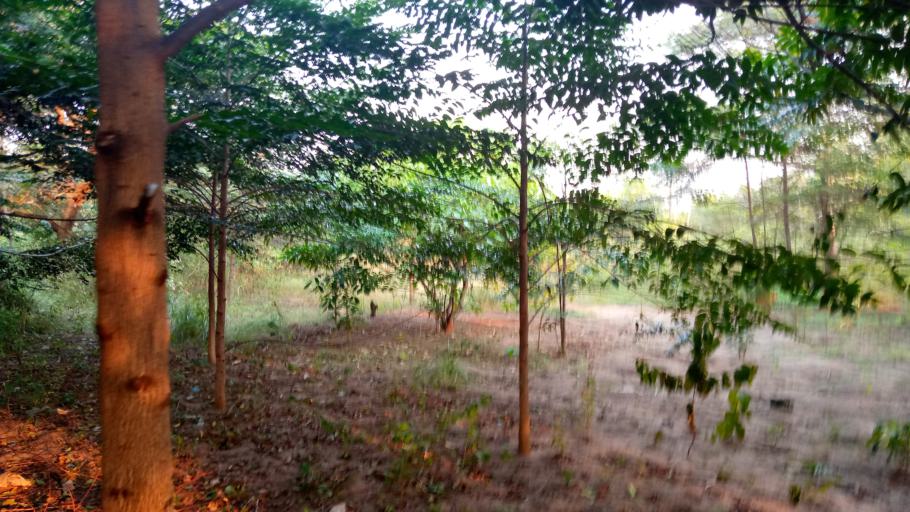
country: CD
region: Bandundu
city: Kikwit
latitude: -5.0150
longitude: 19.4533
